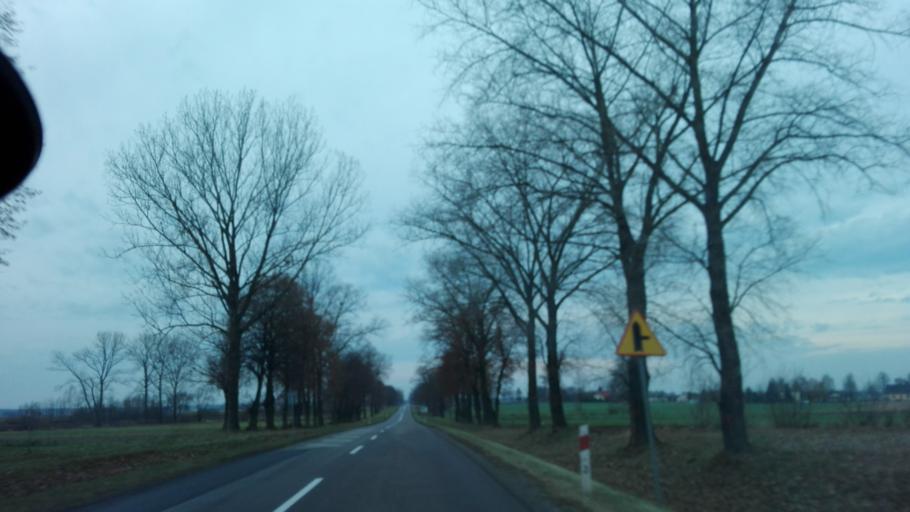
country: PL
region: Lublin Voivodeship
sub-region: Powiat radzynski
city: Wohyn
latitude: 51.7790
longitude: 22.7934
